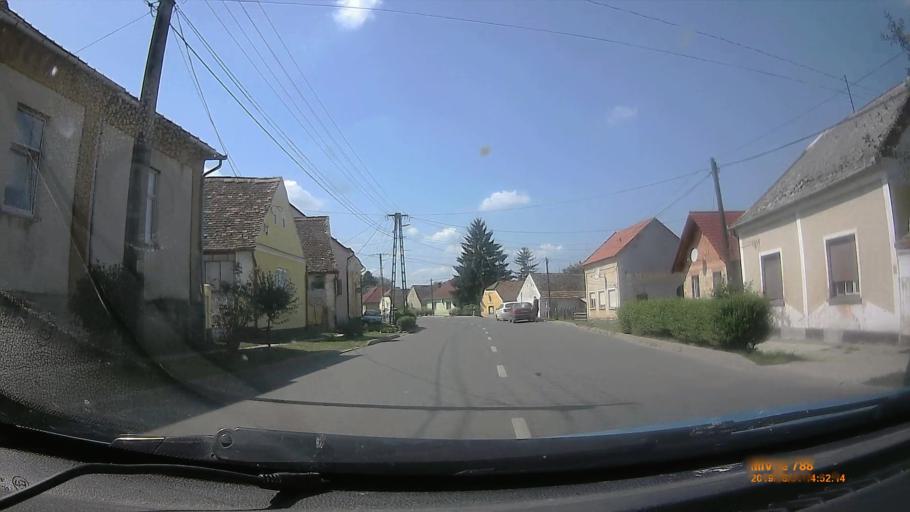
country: HU
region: Baranya
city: Vajszlo
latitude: 45.8576
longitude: 17.9884
